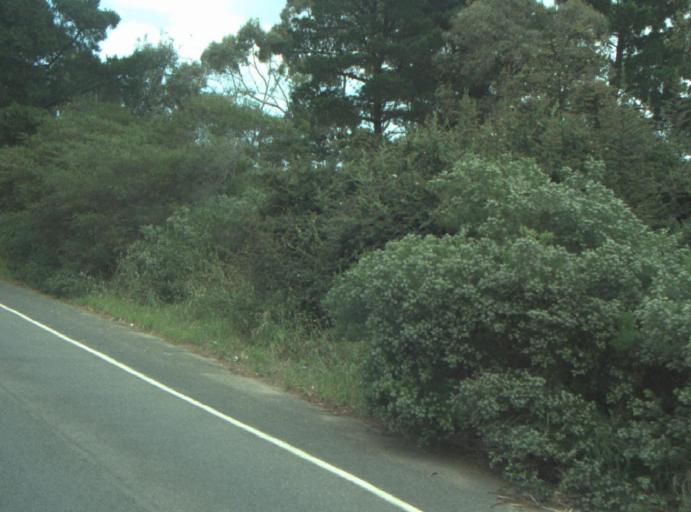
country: AU
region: Victoria
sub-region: Greater Geelong
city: Leopold
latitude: -38.2358
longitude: 144.5023
